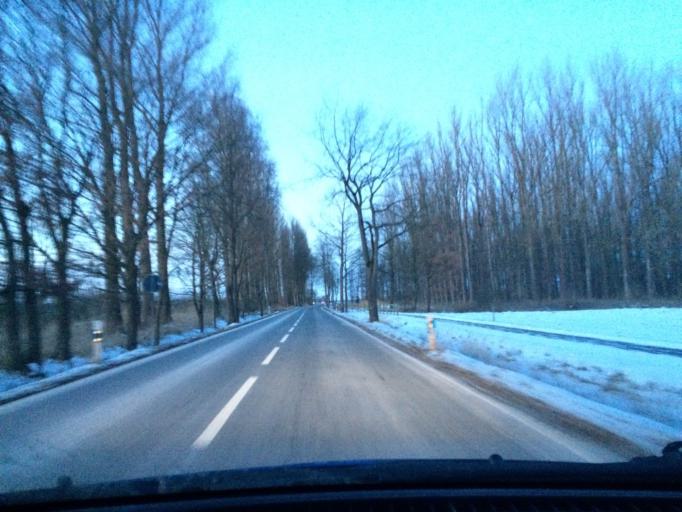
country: DE
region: Lower Saxony
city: Marschacht
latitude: 53.4084
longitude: 10.3606
